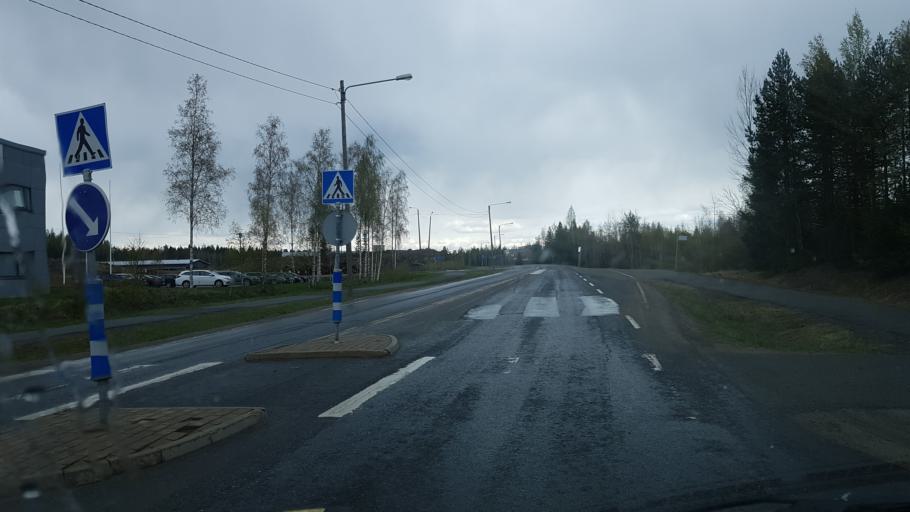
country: FI
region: Pirkanmaa
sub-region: Tampere
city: Pirkkala
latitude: 61.4304
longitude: 23.6214
